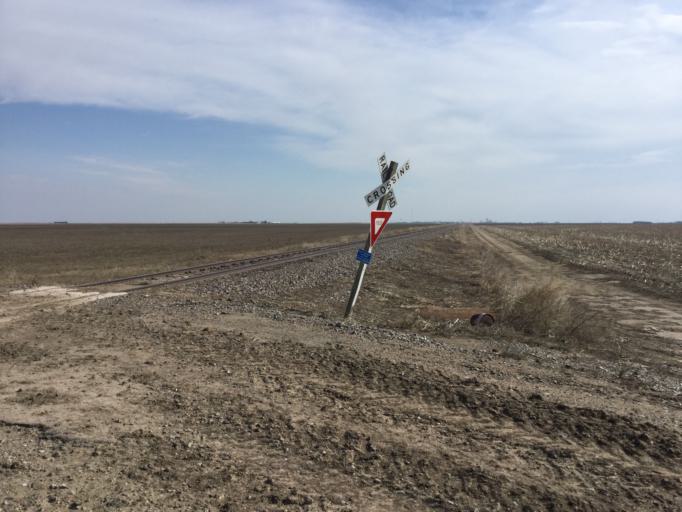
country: US
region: Kansas
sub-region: Lane County
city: Dighton
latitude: 38.5784
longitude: -100.6693
